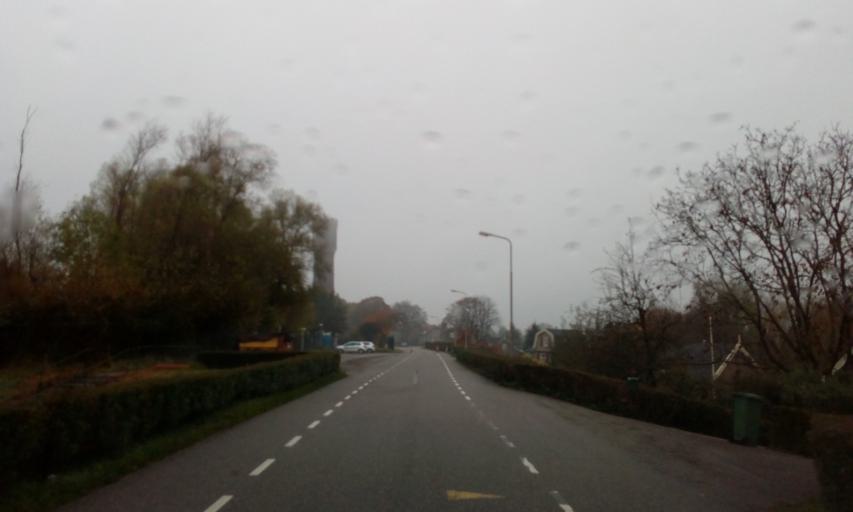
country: NL
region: South Holland
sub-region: Gemeente Alblasserdam
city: Alblasserdam
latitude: 51.8943
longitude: 4.6440
